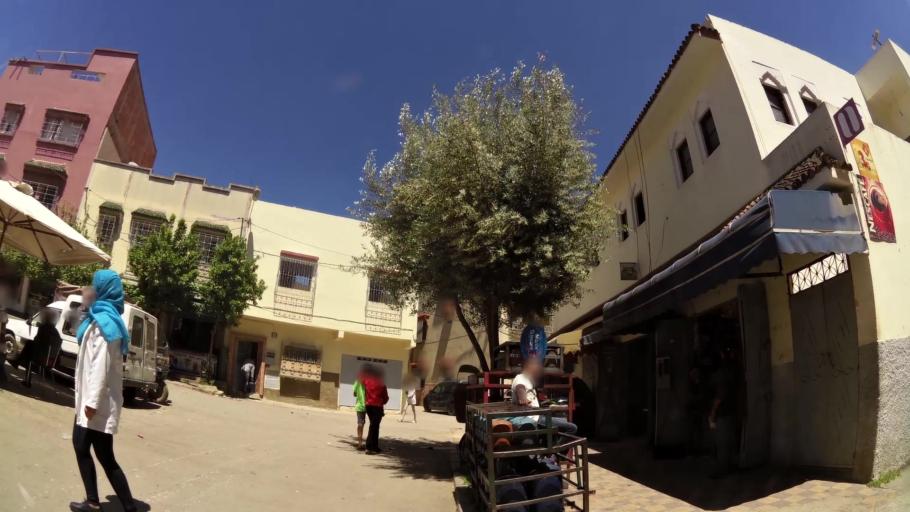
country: MA
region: Meknes-Tafilalet
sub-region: Meknes
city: Meknes
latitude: 33.9053
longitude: -5.5766
